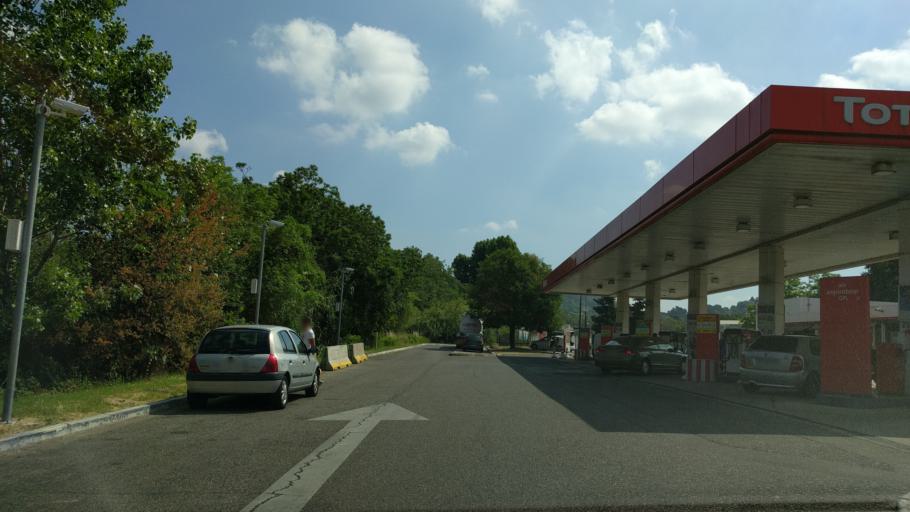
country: FR
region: Provence-Alpes-Cote d'Azur
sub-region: Departement des Bouches-du-Rhone
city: Marseille 11
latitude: 43.2920
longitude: 5.4534
